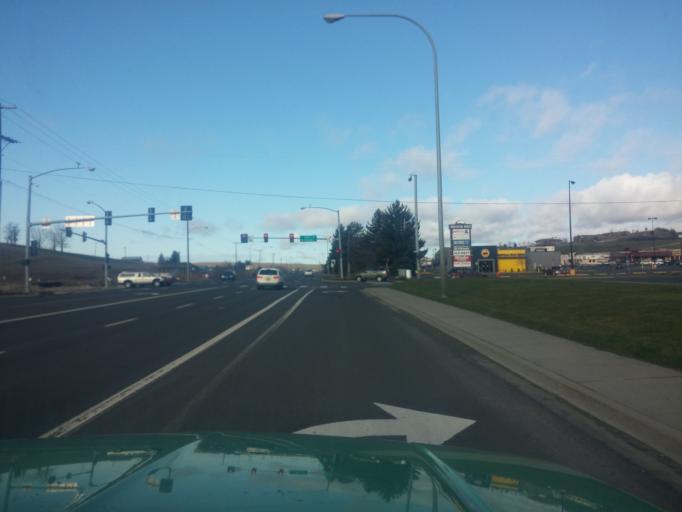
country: US
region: Idaho
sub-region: Latah County
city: Moscow
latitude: 46.7327
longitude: -117.0238
